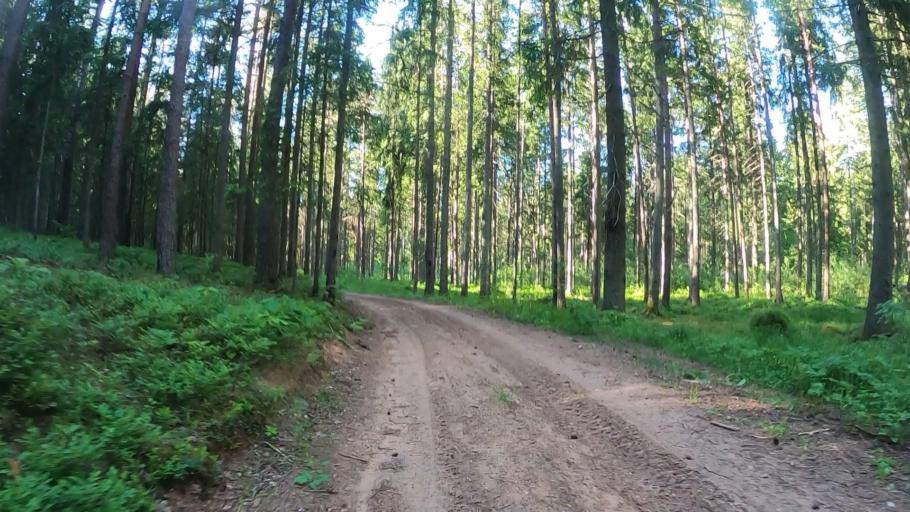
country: LV
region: Ogre
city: Ogre
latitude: 56.8335
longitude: 24.5956
